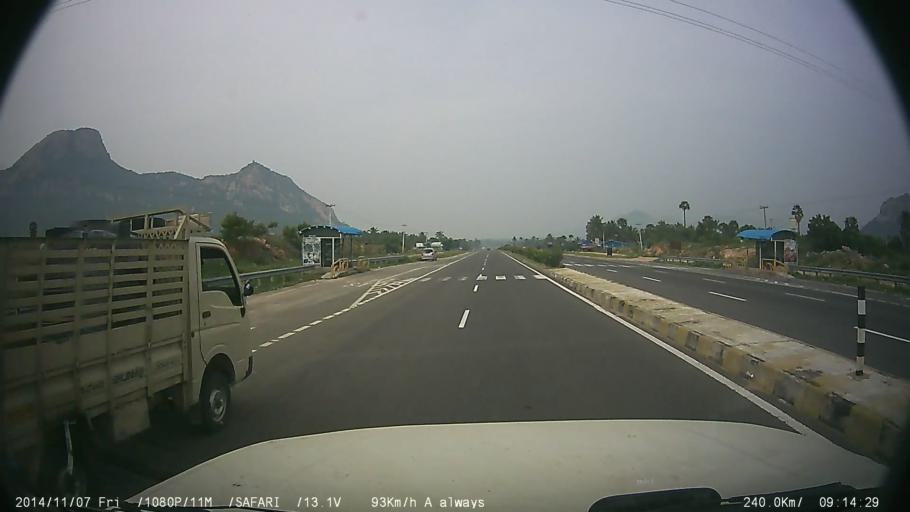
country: IN
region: Tamil Nadu
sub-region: Salem
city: Idappadi
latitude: 11.4938
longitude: 77.8680
